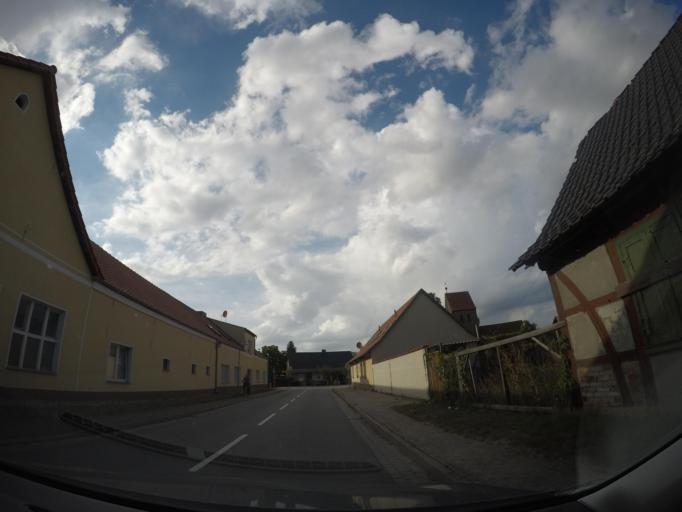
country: DE
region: Saxony-Anhalt
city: Mieste
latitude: 52.4743
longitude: 11.2625
